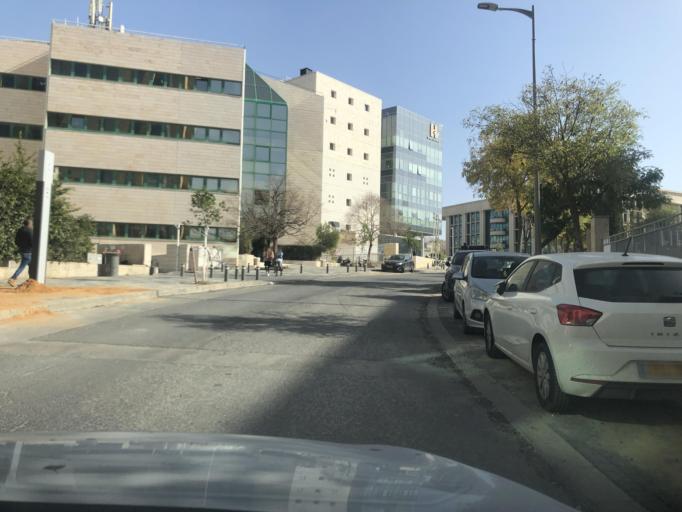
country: IL
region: Jerusalem
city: West Jerusalem
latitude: 31.8043
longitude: 35.2123
